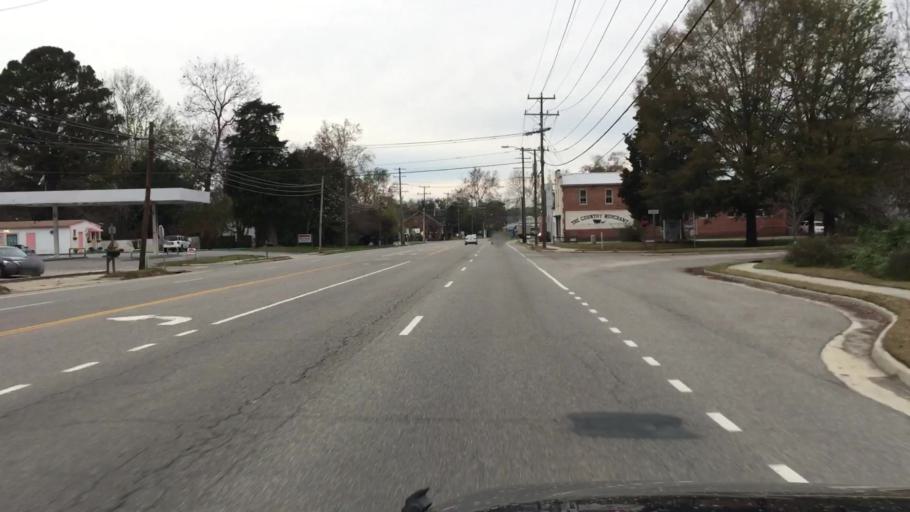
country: US
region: Virginia
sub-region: James City County
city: Williamsburg
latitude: 37.3798
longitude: -76.8037
